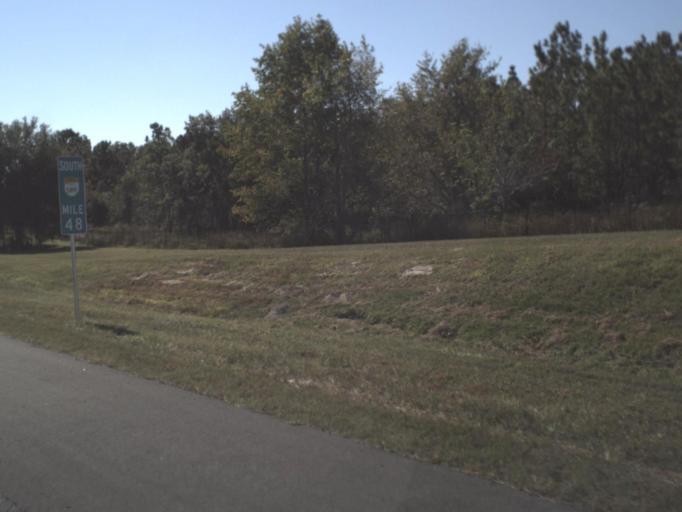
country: US
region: Florida
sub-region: Hernando County
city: Brookridge
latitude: 28.5853
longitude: -82.4808
